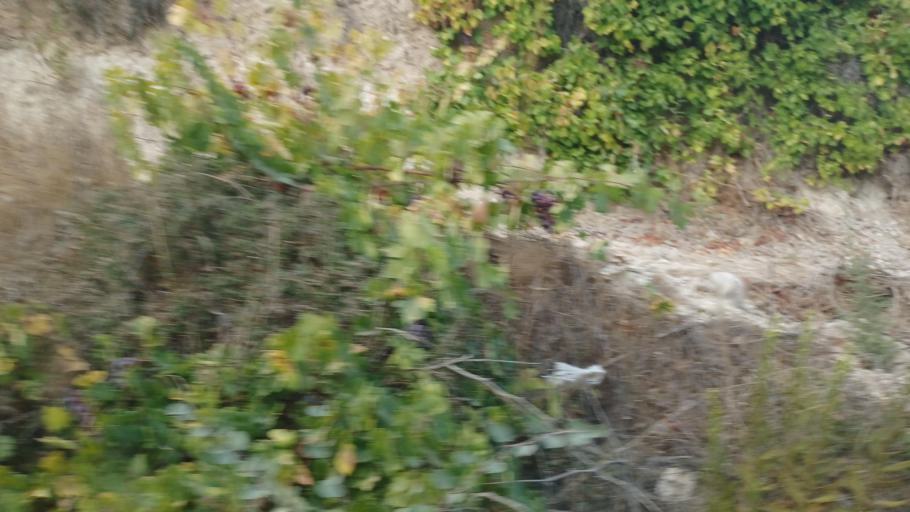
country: CY
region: Pafos
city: Mesogi
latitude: 34.8461
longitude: 32.5422
